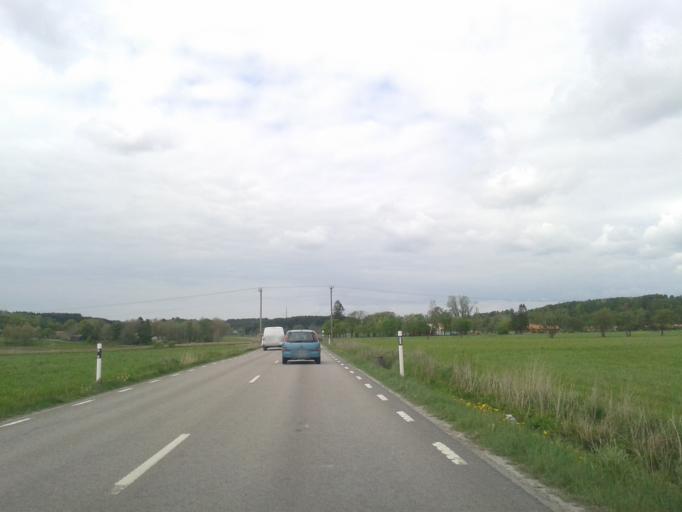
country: SE
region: Vaestra Goetaland
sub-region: Kungalvs Kommun
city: Kode
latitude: 57.8774
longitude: 11.8989
